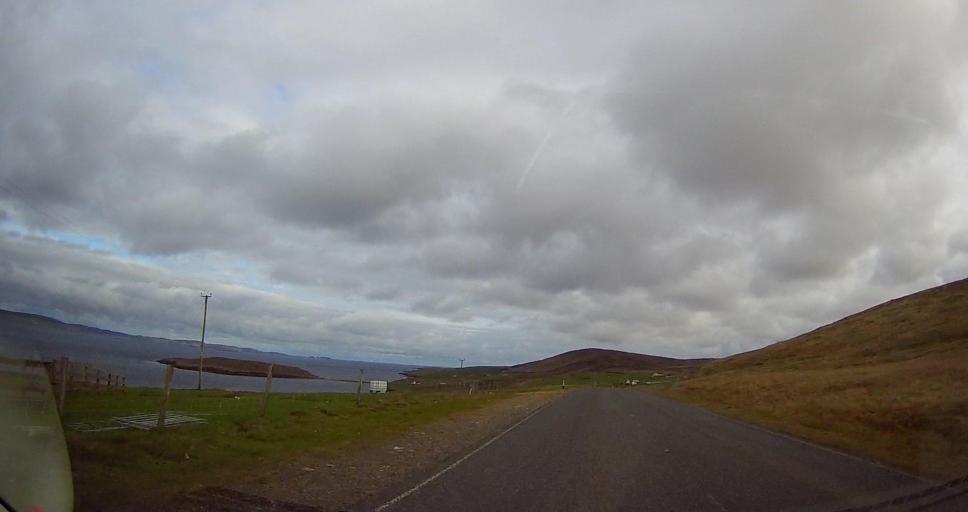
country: GB
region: Scotland
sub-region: Shetland Islands
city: Shetland
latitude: 60.5100
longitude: -1.1663
